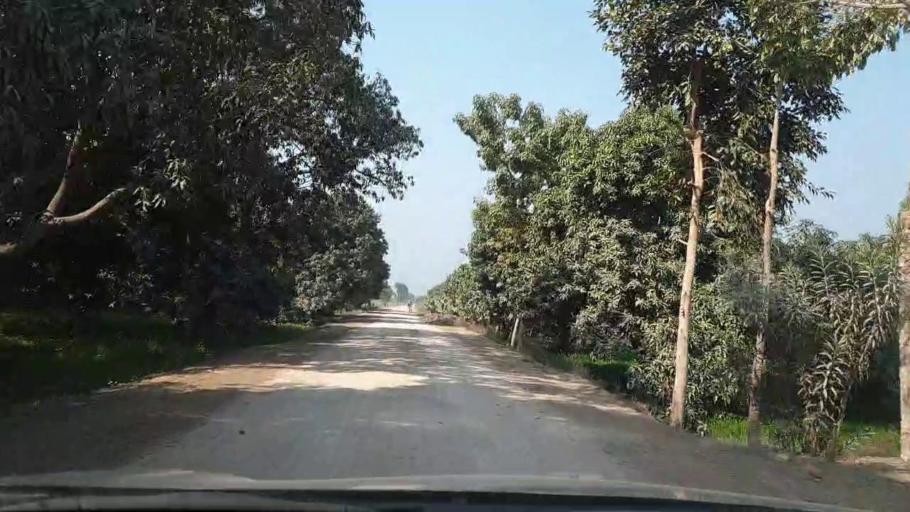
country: PK
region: Sindh
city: Tando Allahyar
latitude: 25.5180
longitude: 68.7496
